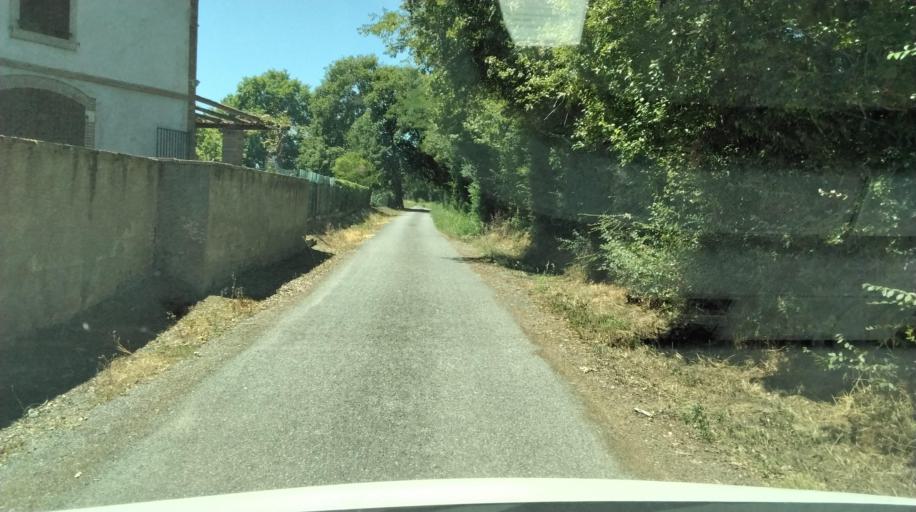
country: FR
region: Midi-Pyrenees
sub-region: Departement de la Haute-Garonne
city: Rieux-Volvestre
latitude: 43.2751
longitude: 1.1366
